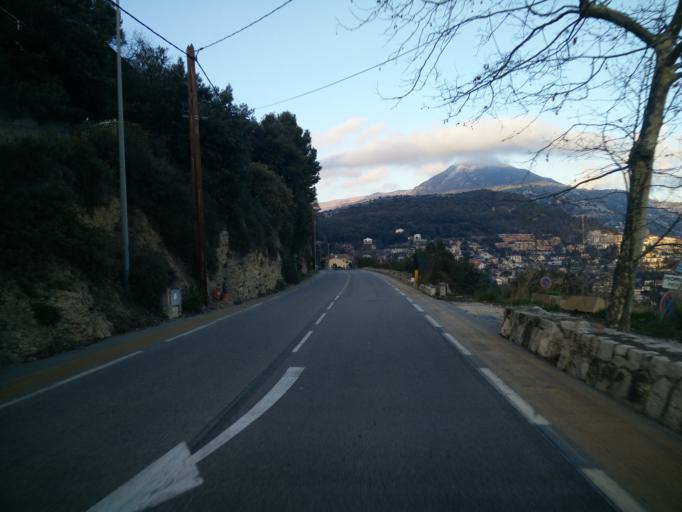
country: FR
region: Provence-Alpes-Cote d'Azur
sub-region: Departement des Alpes-Maritimes
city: La Turbie
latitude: 43.7399
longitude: 7.3901
